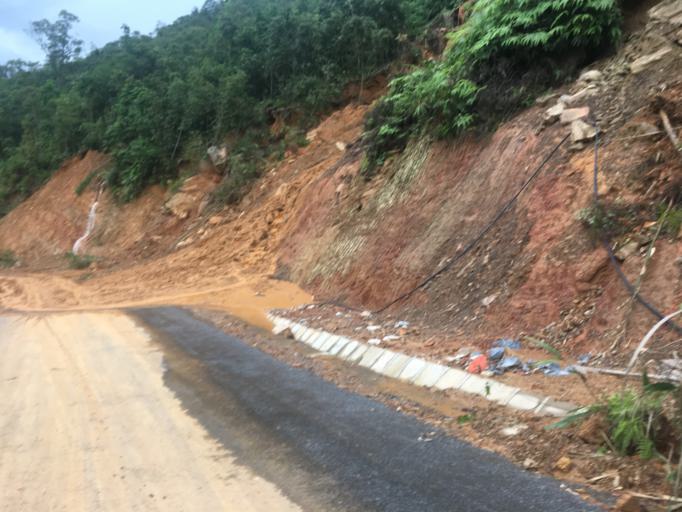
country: VN
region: Ha Giang
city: Thi Tran Tam Son
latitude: 22.9491
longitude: 105.0330
